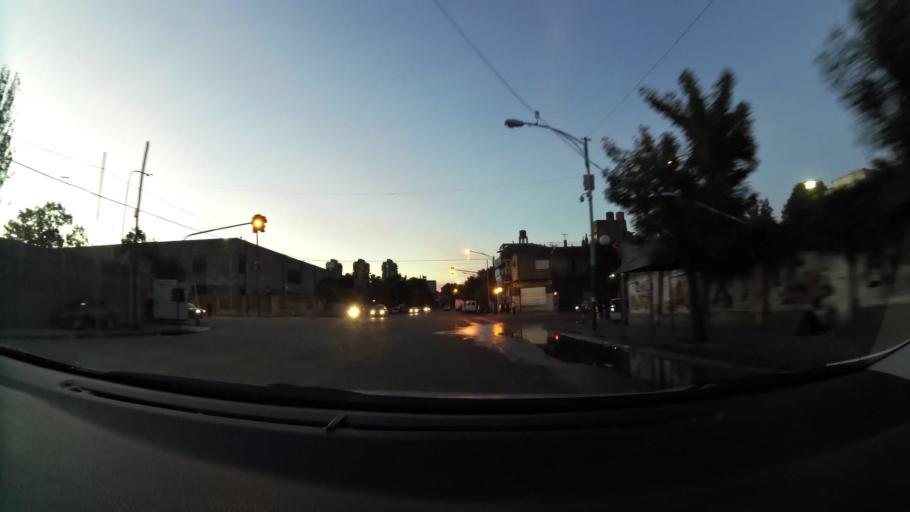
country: AR
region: Buenos Aires F.D.
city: Villa Lugano
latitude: -34.6474
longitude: -58.4489
